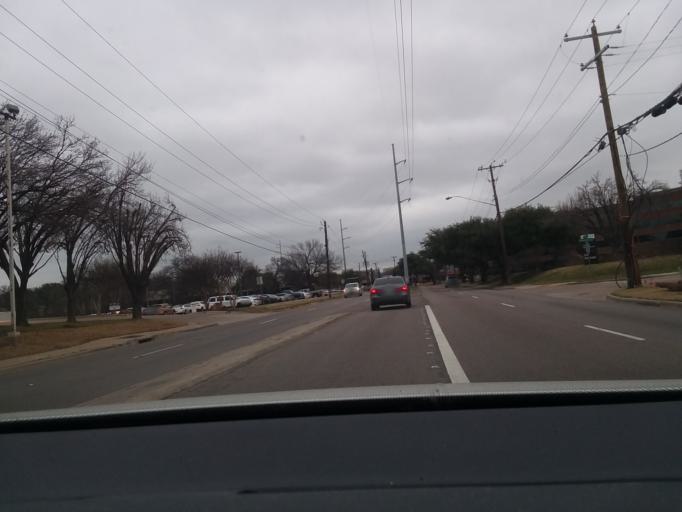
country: US
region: Texas
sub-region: Dallas County
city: University Park
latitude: 32.8265
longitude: -96.8692
